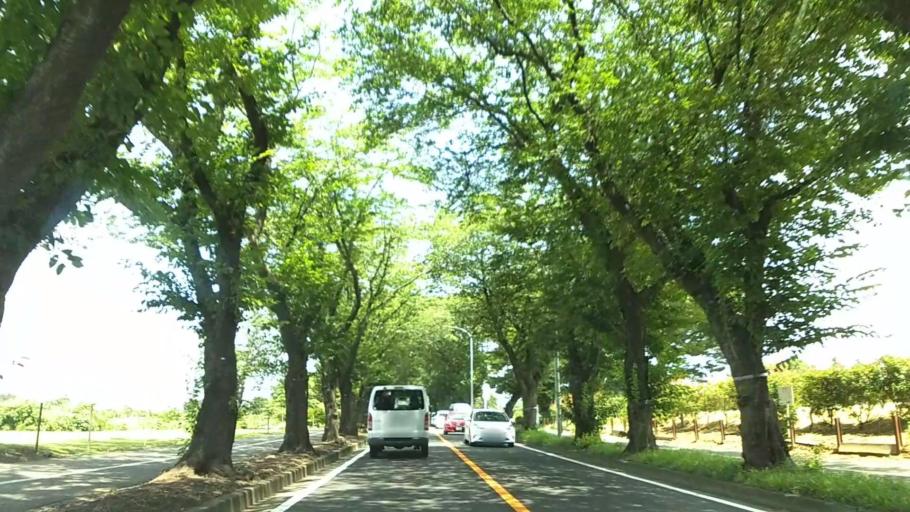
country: JP
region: Kanagawa
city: Minami-rinkan
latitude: 35.4856
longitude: 139.4804
